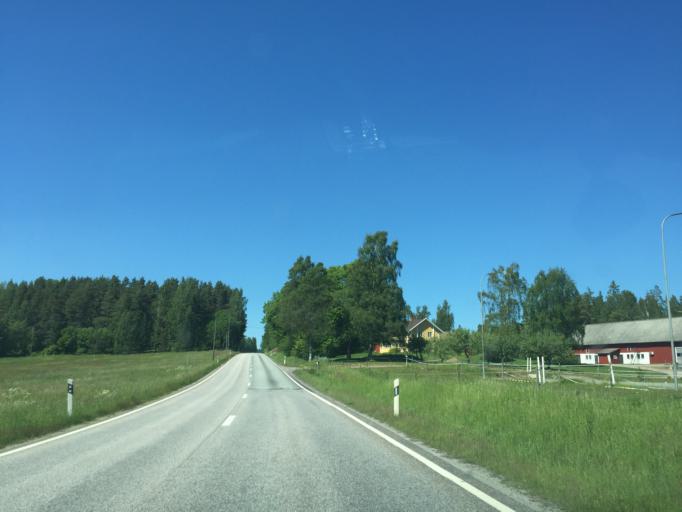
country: SE
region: OEstergoetland
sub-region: Motala Kommun
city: Ryd
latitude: 58.6976
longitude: 14.9674
